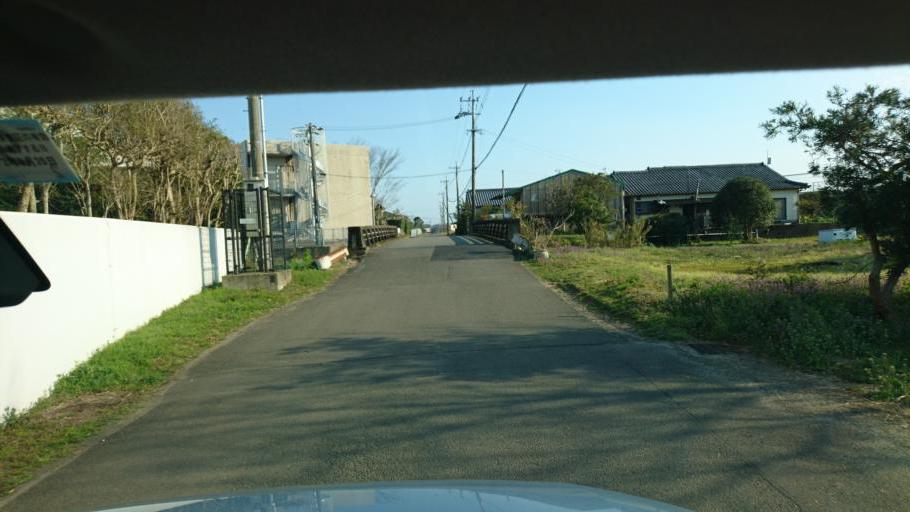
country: JP
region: Miyazaki
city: Miyazaki-shi
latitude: 32.0054
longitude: 131.4395
